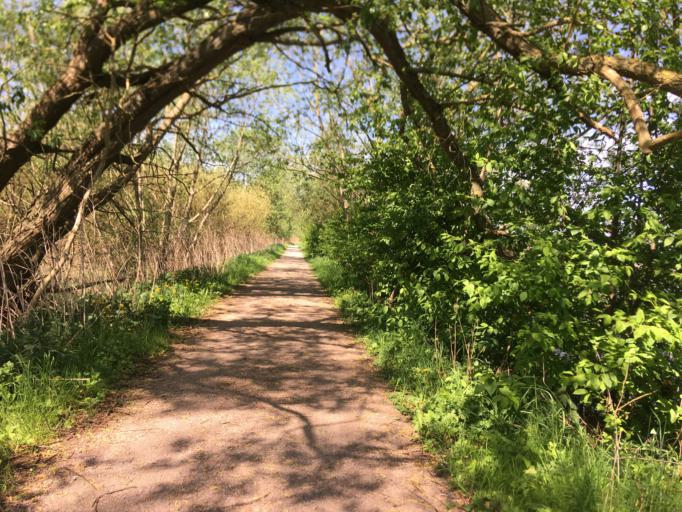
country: SE
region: Skane
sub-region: Staffanstorps Kommun
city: Hjaerup
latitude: 55.6953
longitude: 13.1582
